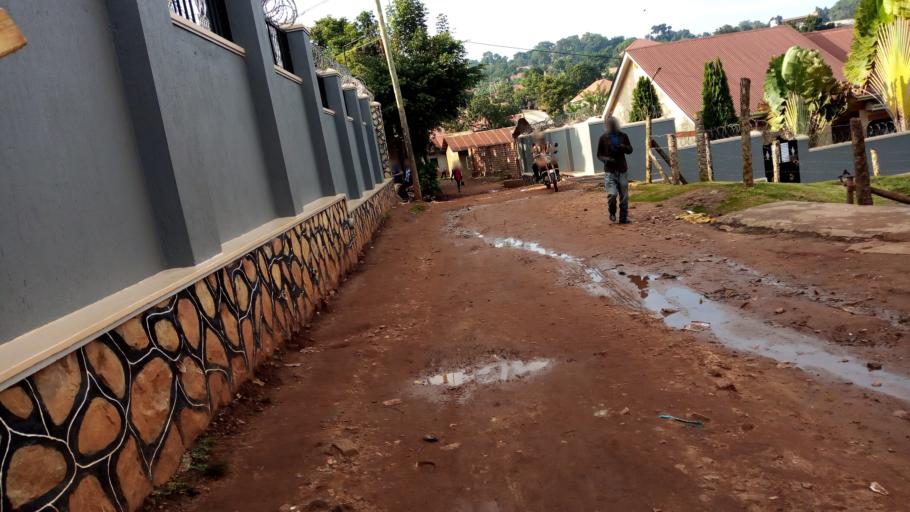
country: UG
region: Central Region
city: Kampala Central Division
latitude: 0.3745
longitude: 32.5520
